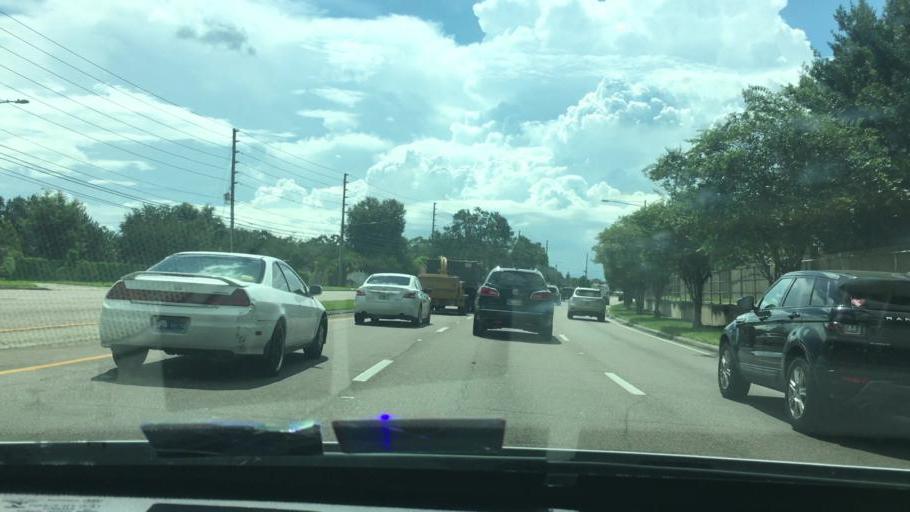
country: US
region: Florida
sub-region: Seminole County
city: Goldenrod
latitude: 28.5975
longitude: -81.2624
